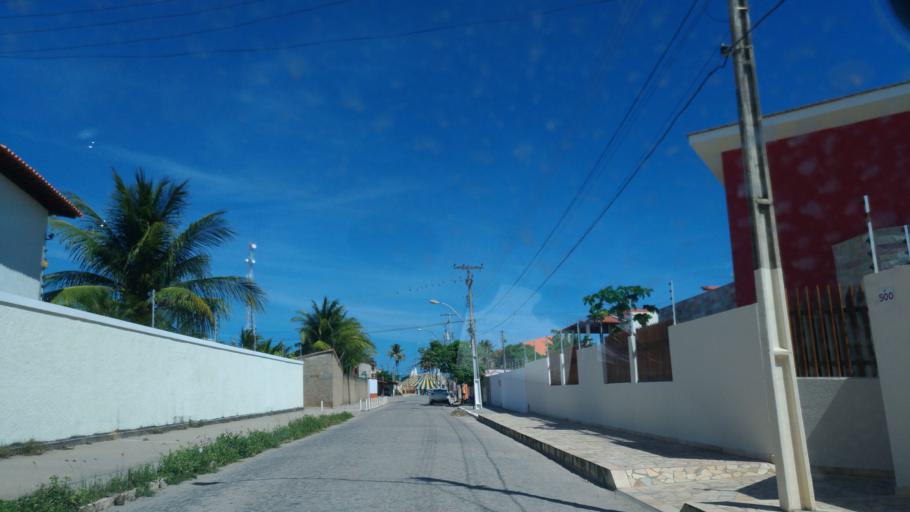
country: BR
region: Alagoas
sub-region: Marechal Deodoro
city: Marechal Deodoro
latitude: -9.7679
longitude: -35.8456
